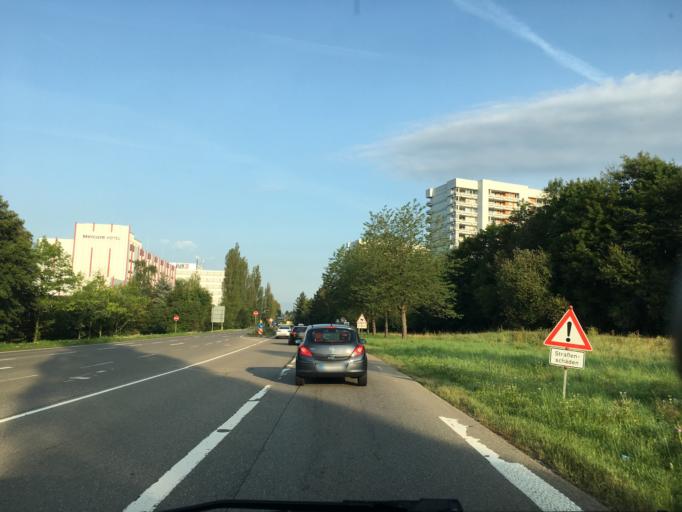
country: DE
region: Baden-Wuerttemberg
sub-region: Regierungsbezirk Stuttgart
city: Sindelfingen
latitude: 48.7048
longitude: 9.0420
